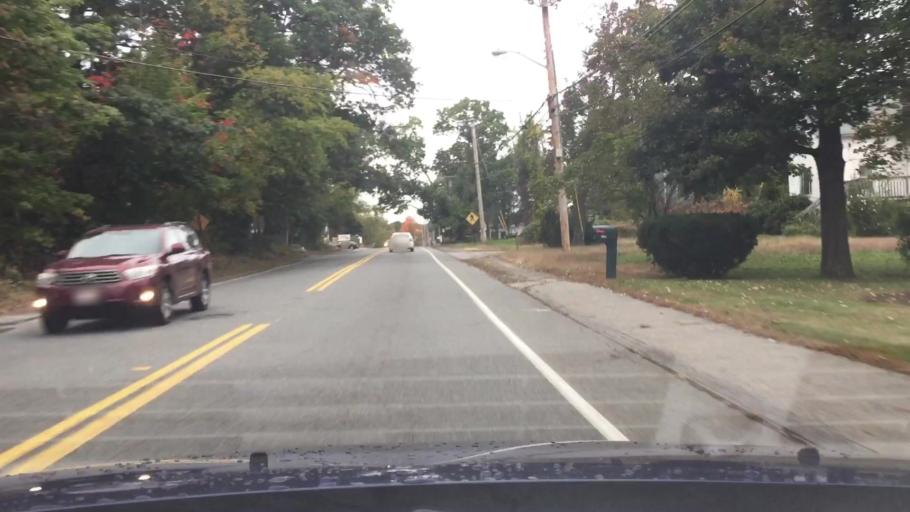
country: US
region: Massachusetts
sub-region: Middlesex County
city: Tyngsboro
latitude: 42.6798
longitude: -71.3656
